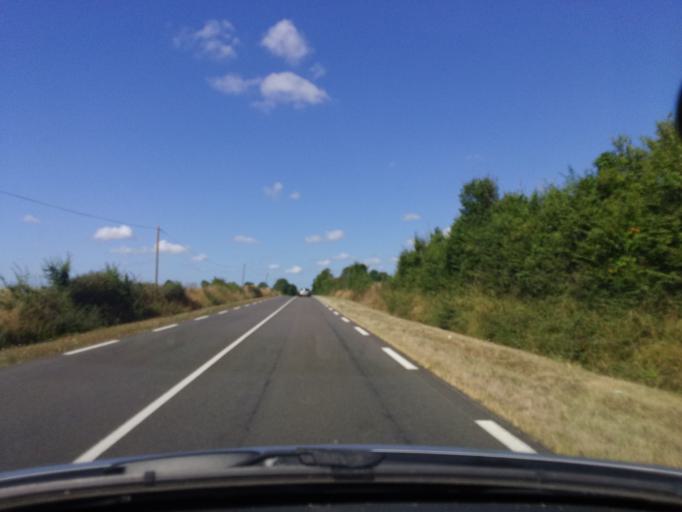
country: FR
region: Pays de la Loire
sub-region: Departement de la Vendee
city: Moutiers-les-Mauxfaits
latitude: 46.4562
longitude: -1.3816
